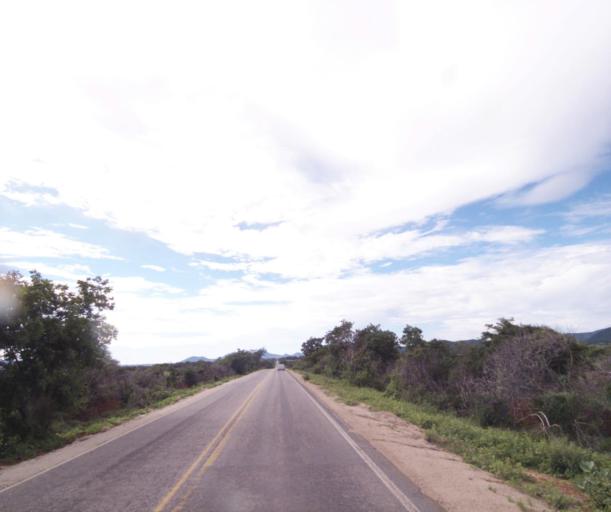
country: BR
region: Bahia
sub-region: Guanambi
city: Guanambi
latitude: -14.4141
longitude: -42.7363
